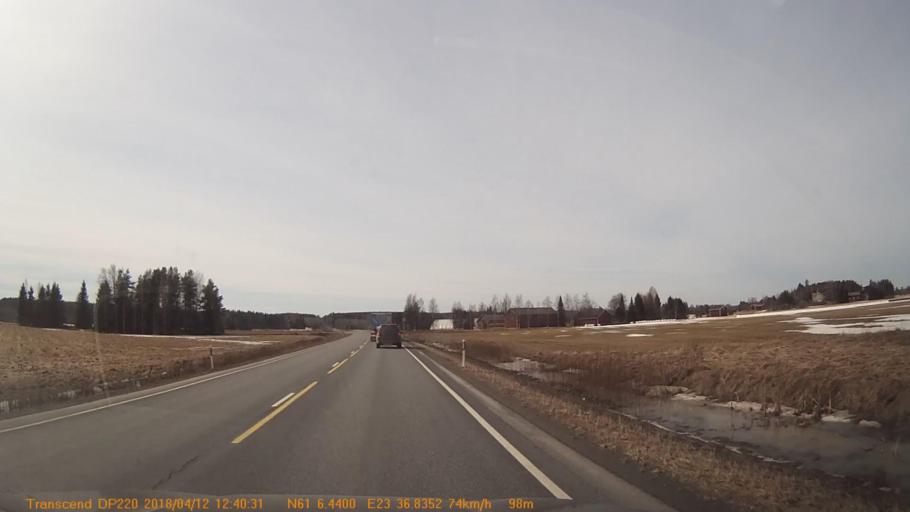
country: FI
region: Pirkanmaa
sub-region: Etelae-Pirkanmaa
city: Urjala
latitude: 61.1068
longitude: 23.6137
